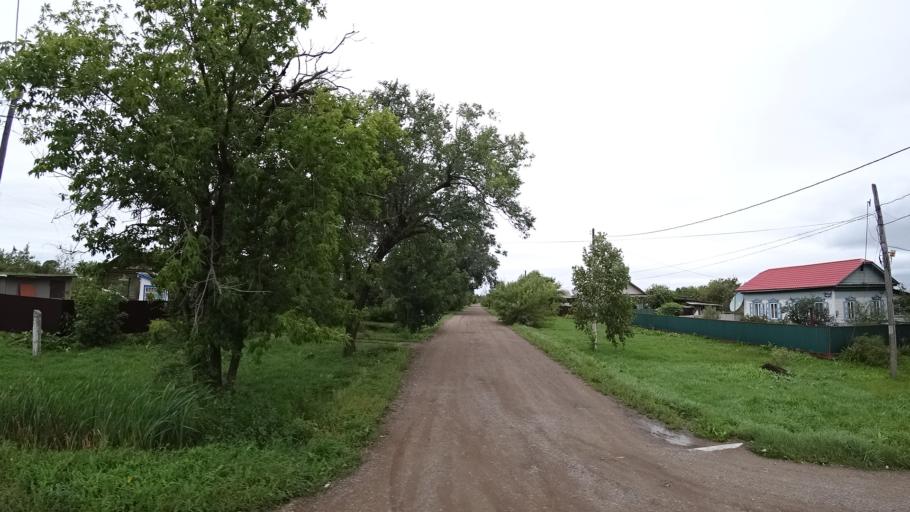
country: RU
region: Primorskiy
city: Chernigovka
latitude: 44.3401
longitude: 132.5629
